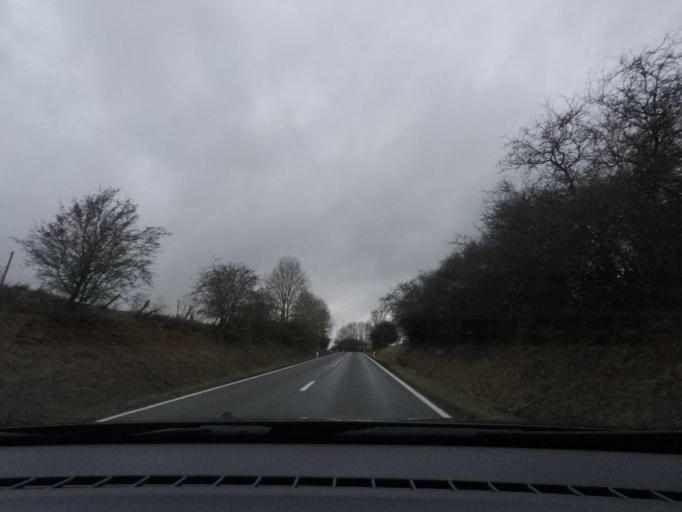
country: BE
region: Wallonia
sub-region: Province du Luxembourg
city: Tintigny
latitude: 49.6984
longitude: 5.5281
